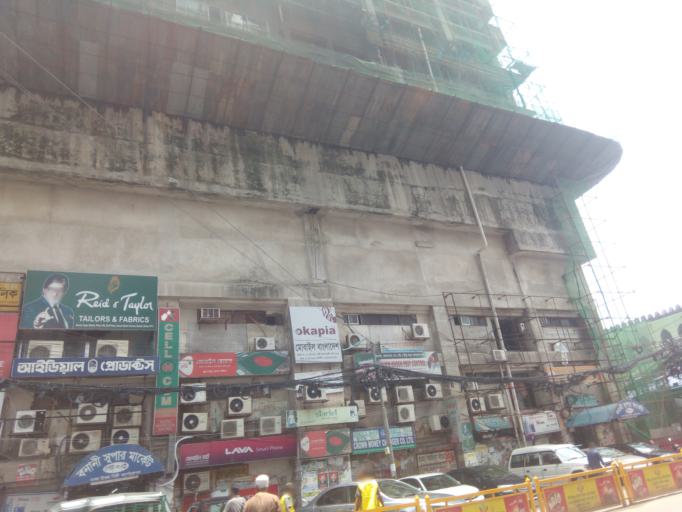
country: BD
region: Dhaka
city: Paltan
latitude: 23.7934
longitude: 90.4058
